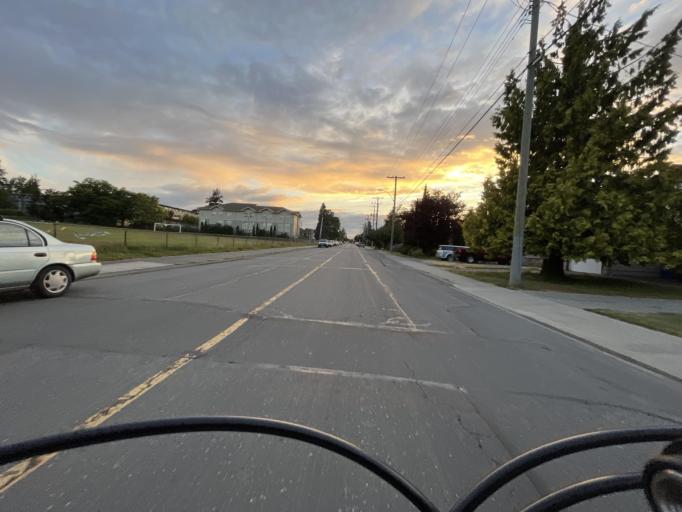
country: CA
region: British Columbia
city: Victoria
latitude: 48.4269
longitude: -123.4051
